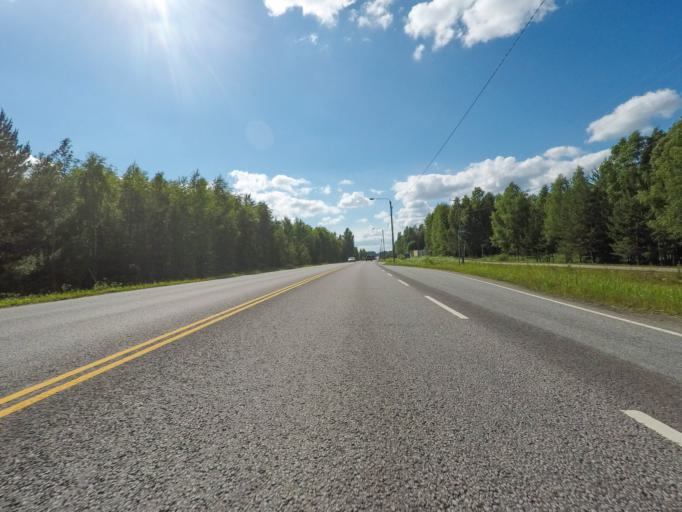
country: FI
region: Southern Savonia
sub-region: Savonlinna
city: Savonlinna
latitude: 61.8770
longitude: 29.0016
